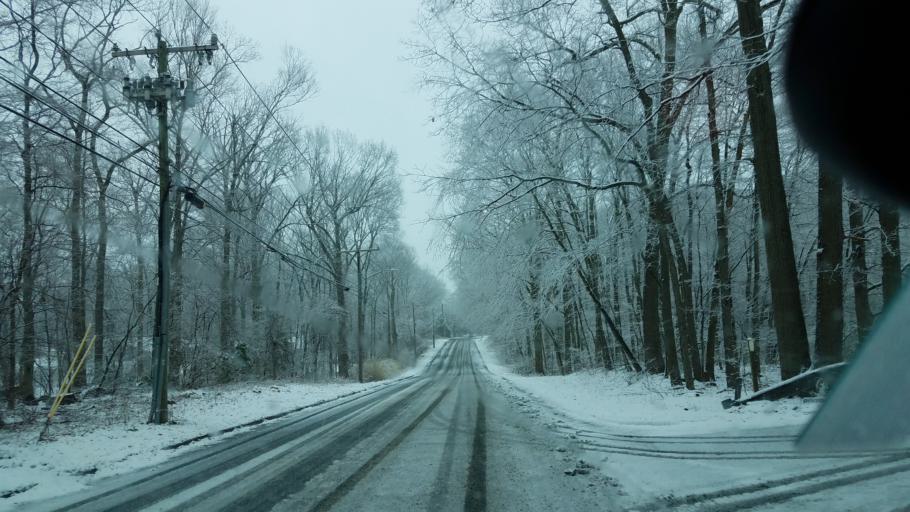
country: US
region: Connecticut
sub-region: New Haven County
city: Cheshire
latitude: 41.4883
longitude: -72.9280
